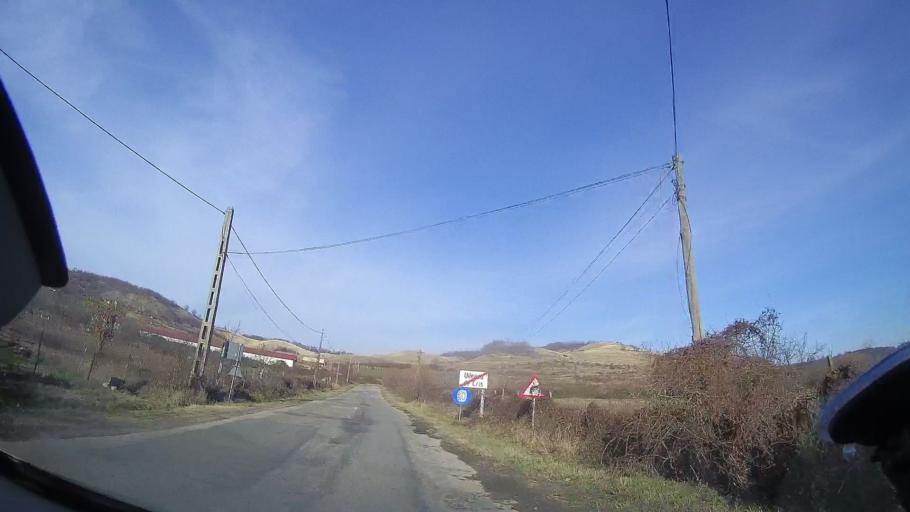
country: RO
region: Bihor
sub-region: Comuna Tileagd
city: Tileagd
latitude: 47.0813
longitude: 22.2225
